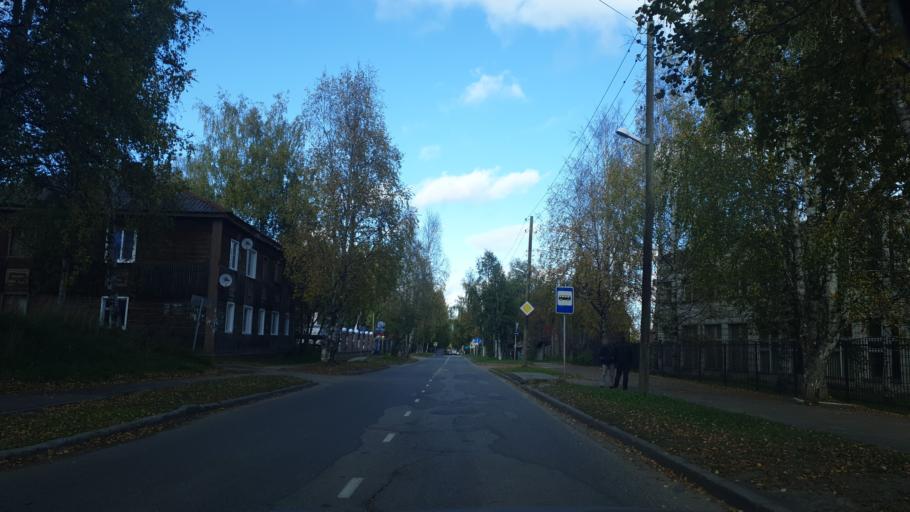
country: RU
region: Komi Republic
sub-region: Syktyvdinskiy Rayon
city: Syktyvkar
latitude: 61.6599
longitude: 50.8384
